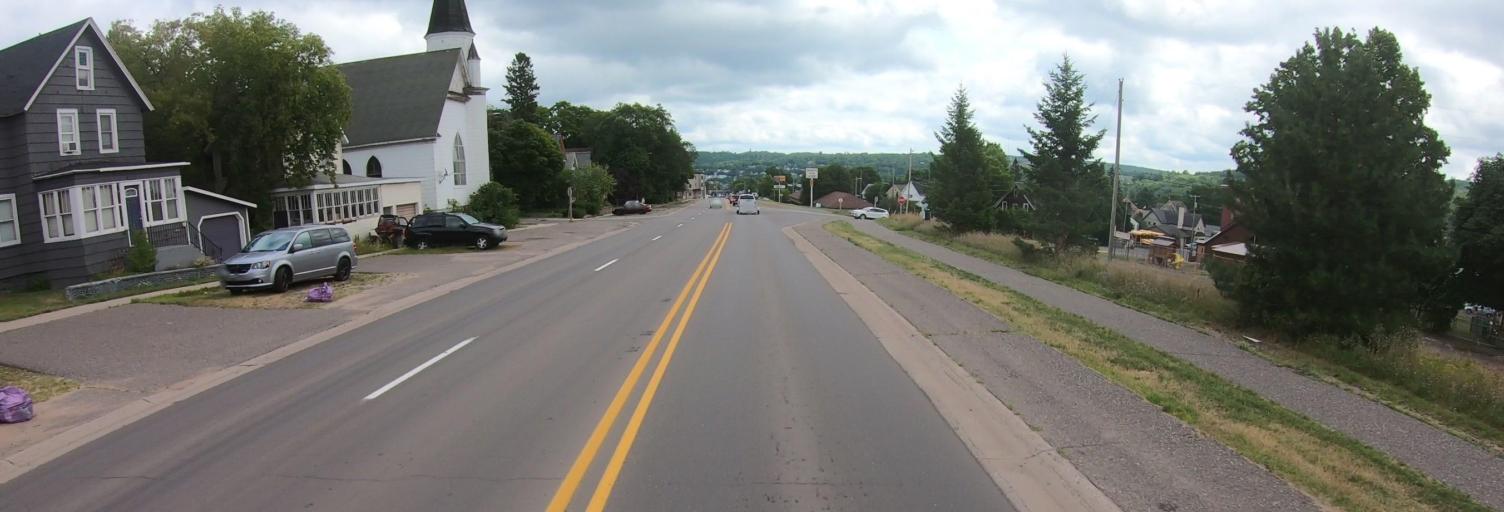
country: US
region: Michigan
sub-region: Houghton County
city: Hancock
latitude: 47.1289
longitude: -88.5983
